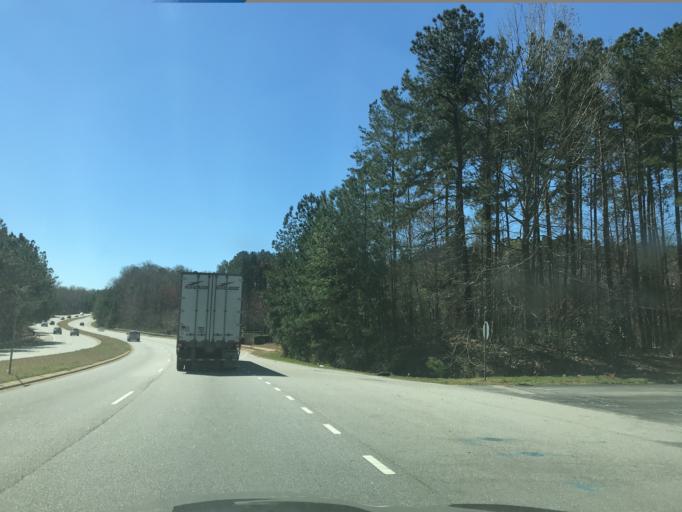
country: US
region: North Carolina
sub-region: Wake County
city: Raleigh
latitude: 35.7408
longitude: -78.6411
